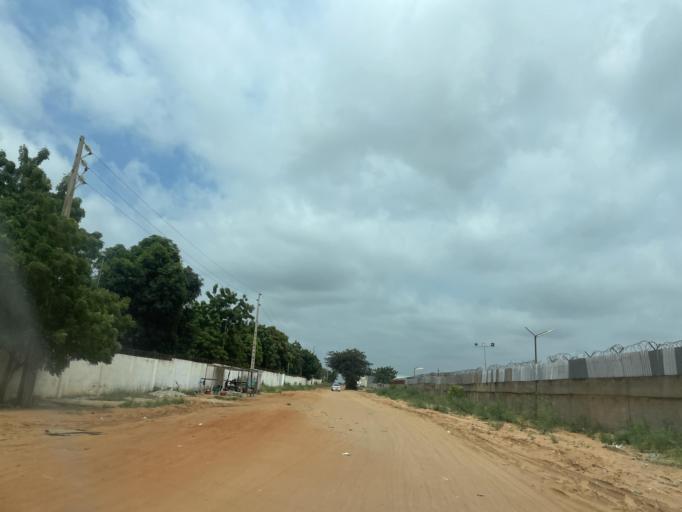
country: AO
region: Luanda
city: Luanda
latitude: -8.9333
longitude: 13.3928
